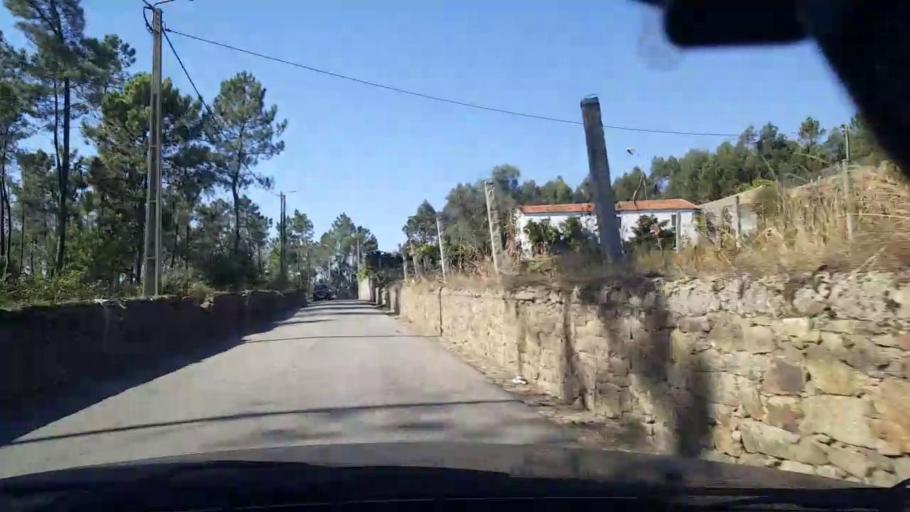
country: PT
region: Porto
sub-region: Vila do Conde
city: Arvore
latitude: 41.3649
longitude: -8.6461
